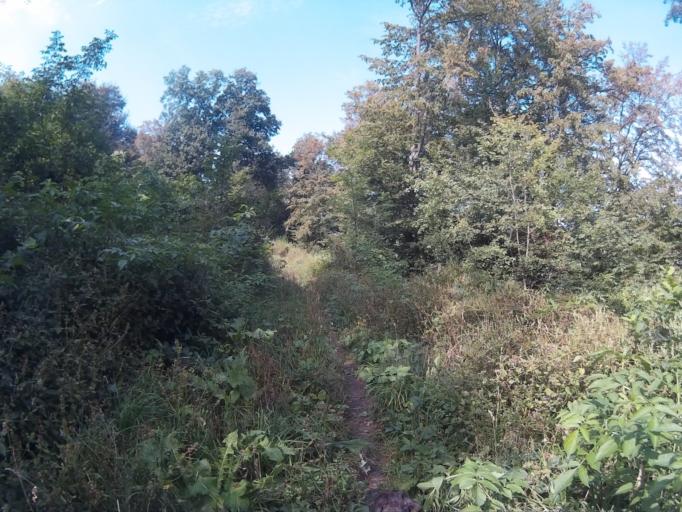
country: HU
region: Vas
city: Koszeg
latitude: 47.4008
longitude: 16.5321
